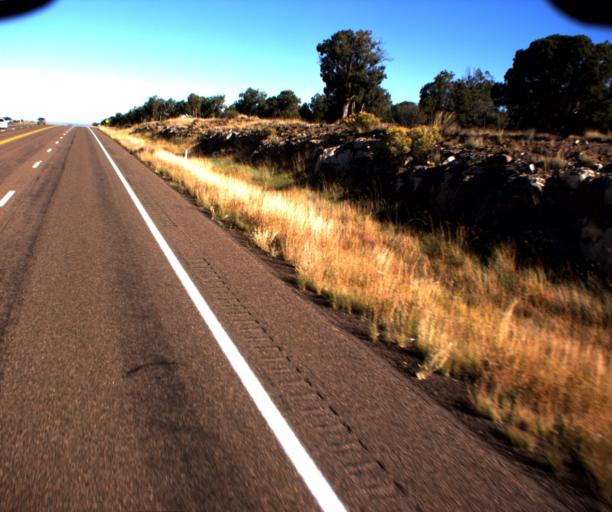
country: US
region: Arizona
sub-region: Navajo County
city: White Mountain Lake
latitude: 34.3329
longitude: -110.0477
